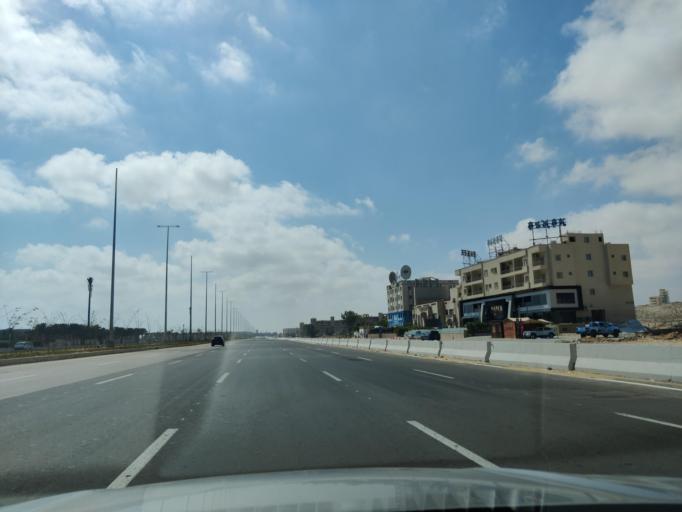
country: EG
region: Muhafazat Matruh
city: Al `Alamayn
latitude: 30.9635
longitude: 28.7527
